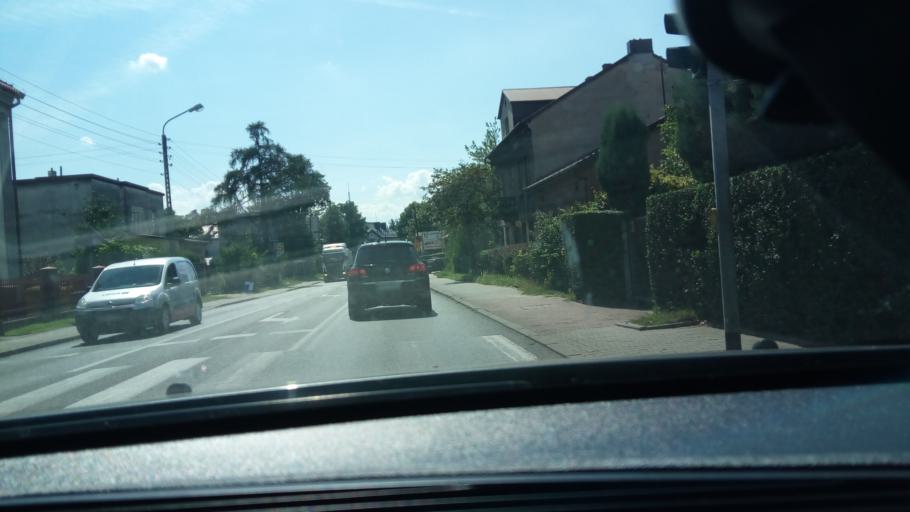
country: PL
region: Lesser Poland Voivodeship
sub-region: Powiat chrzanowski
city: Chrzanow
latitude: 50.1416
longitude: 19.3978
